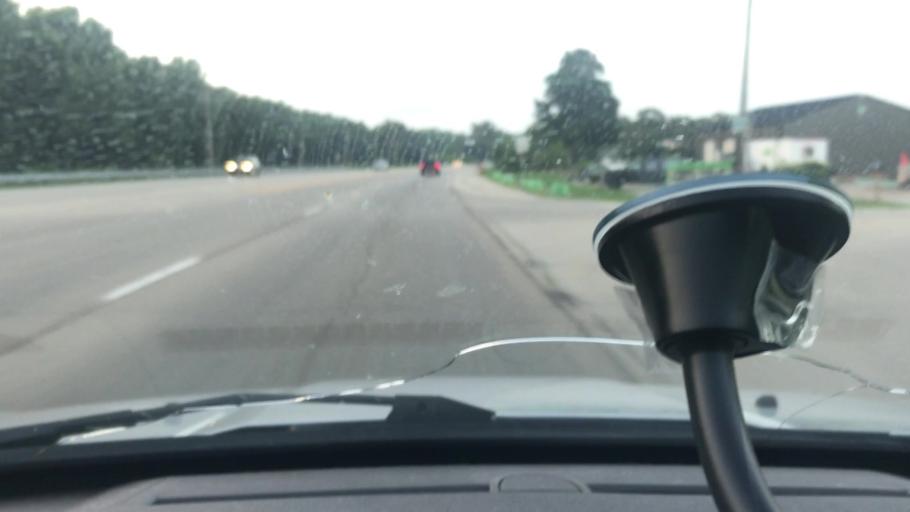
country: US
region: Illinois
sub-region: Tazewell County
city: North Pekin
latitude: 40.6090
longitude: -89.6346
